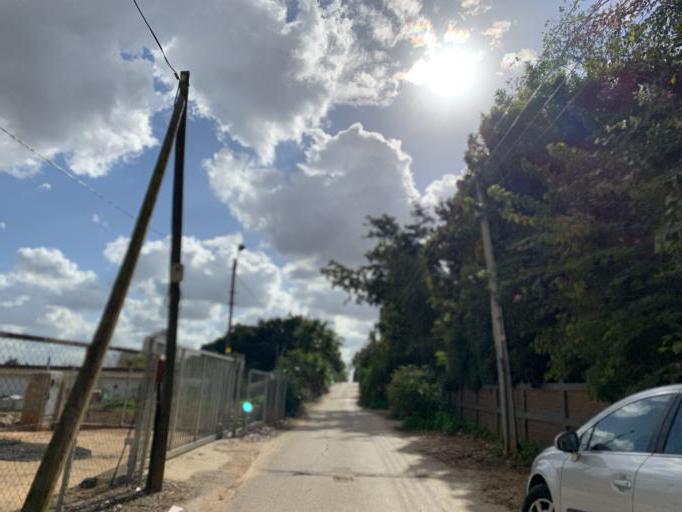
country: IL
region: Central District
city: Hod HaSharon
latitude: 32.1695
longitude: 34.8913
